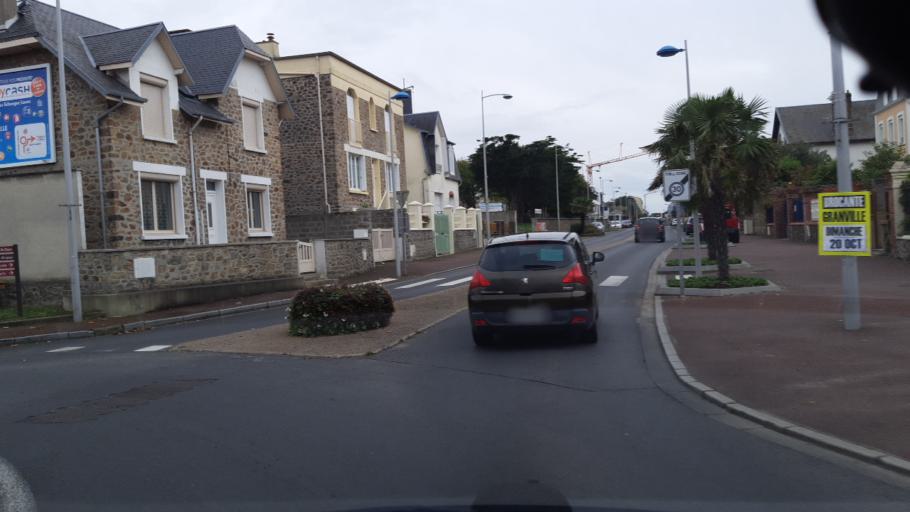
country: FR
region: Lower Normandy
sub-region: Departement de la Manche
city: Donville-les-Bains
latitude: 48.8452
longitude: -1.5839
